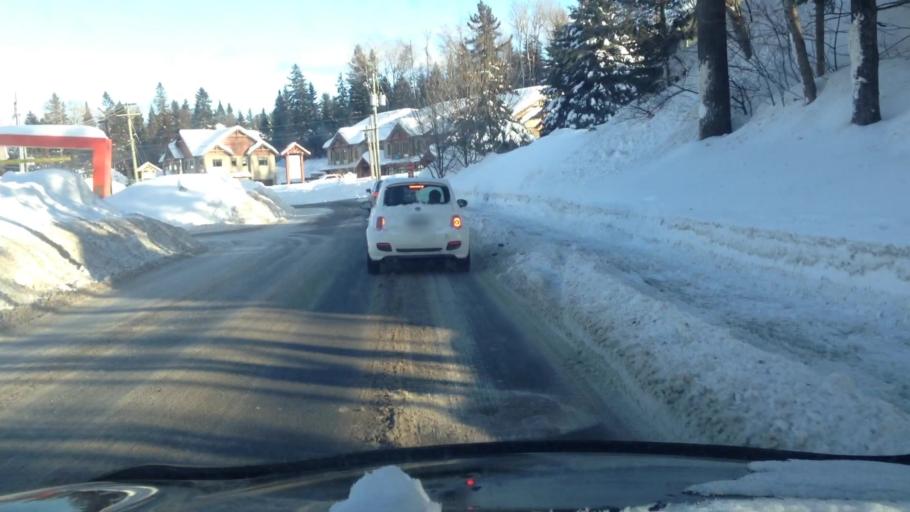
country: CA
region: Quebec
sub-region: Laurentides
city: Saint-Sauveur
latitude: 45.8890
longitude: -74.1467
